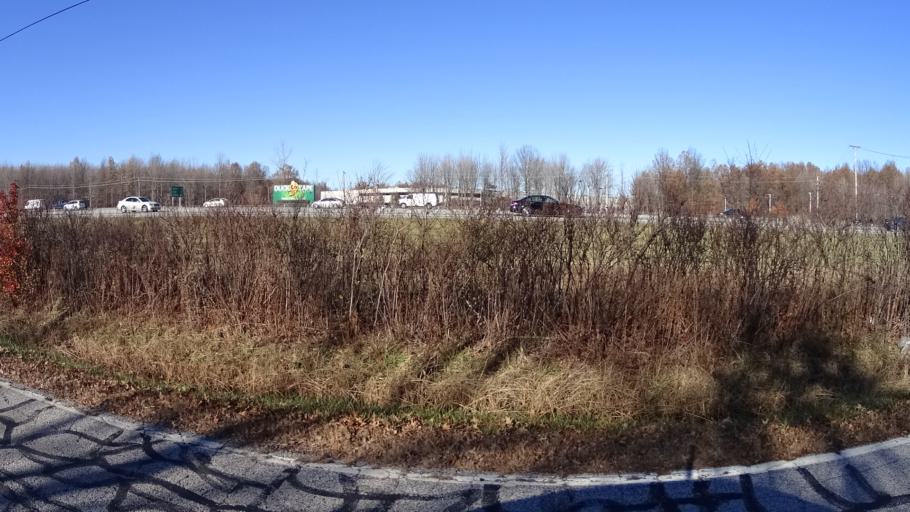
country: US
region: Ohio
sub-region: Lorain County
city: Avon Center
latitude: 41.4682
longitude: -81.9727
